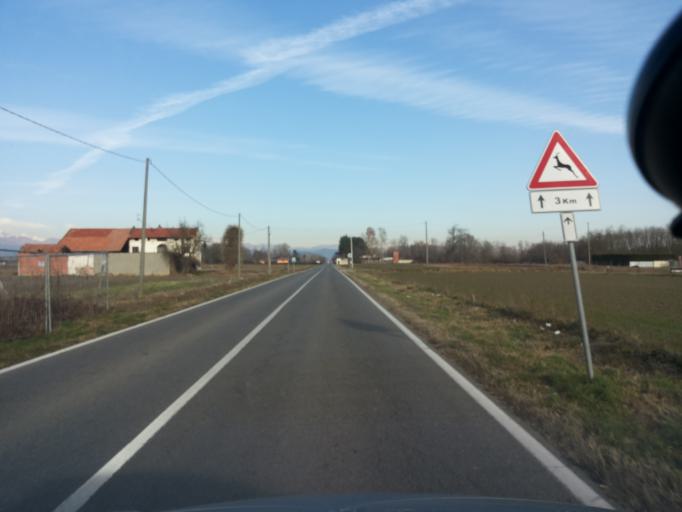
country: IT
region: Piedmont
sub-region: Provincia di Vercelli
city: Arborio
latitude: 45.5045
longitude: 8.3888
